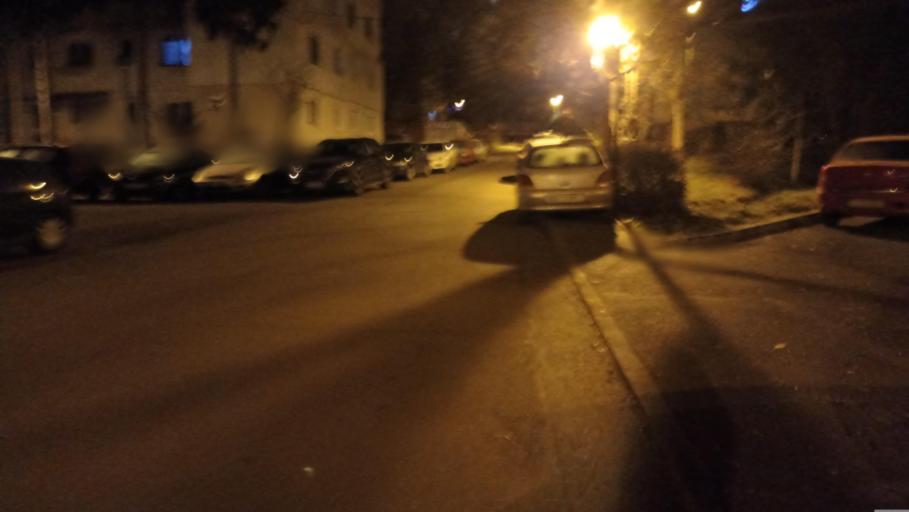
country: RO
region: Cluj
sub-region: Municipiul Cluj-Napoca
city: Cluj-Napoca
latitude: 46.7504
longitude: 23.5505
